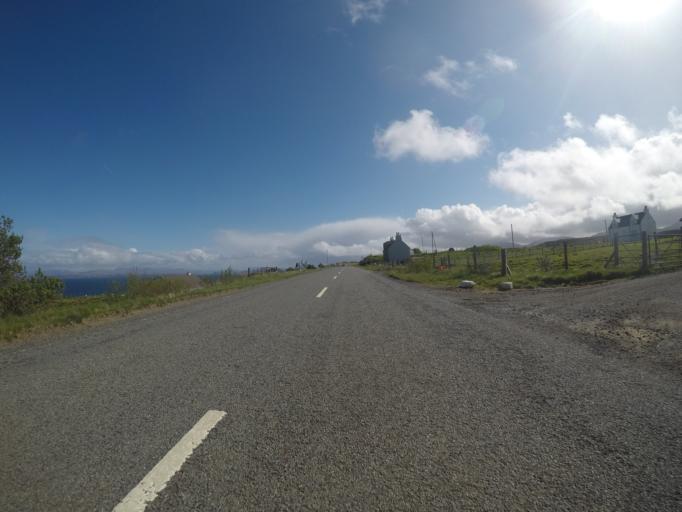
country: GB
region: Scotland
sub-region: Highland
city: Portree
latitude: 57.5969
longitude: -6.1619
